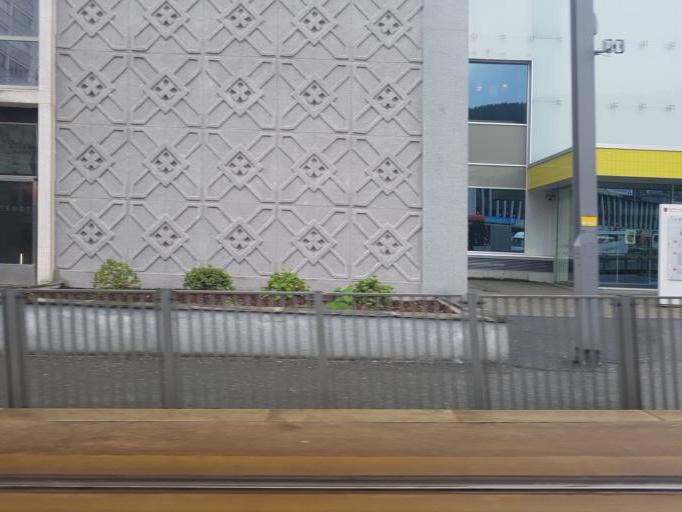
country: NO
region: Hordaland
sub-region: Bergen
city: Bergen
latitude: 60.3748
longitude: 5.3403
